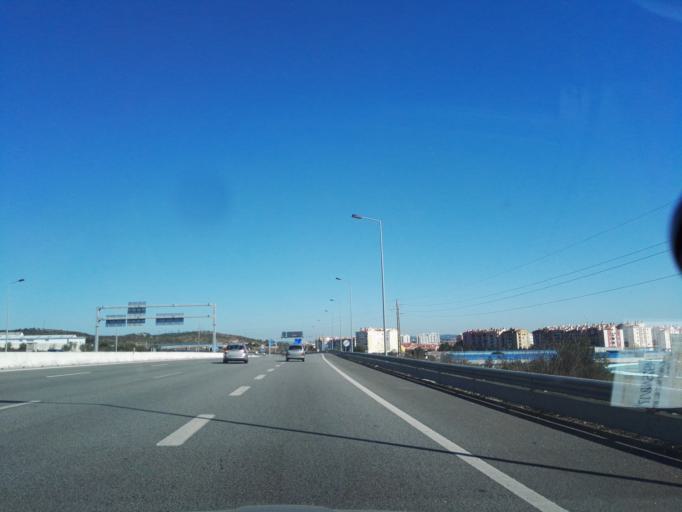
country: PT
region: Lisbon
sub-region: Sintra
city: Sintra
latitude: 38.7849
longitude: -9.3610
